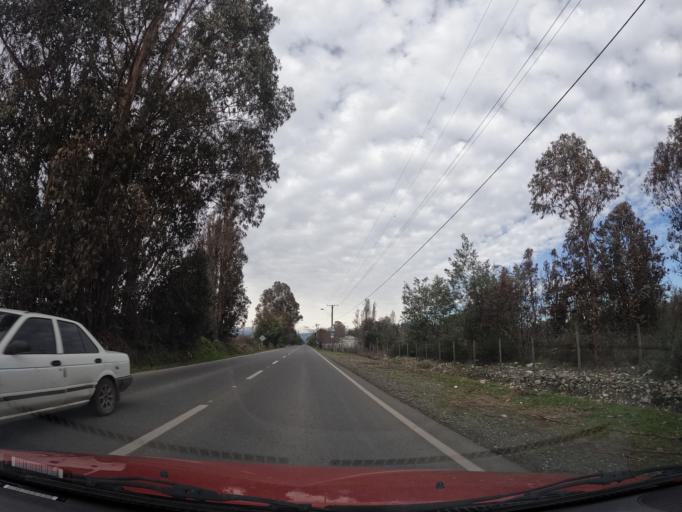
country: CL
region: Maule
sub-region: Provincia de Linares
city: Linares
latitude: -35.8874
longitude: -71.5305
